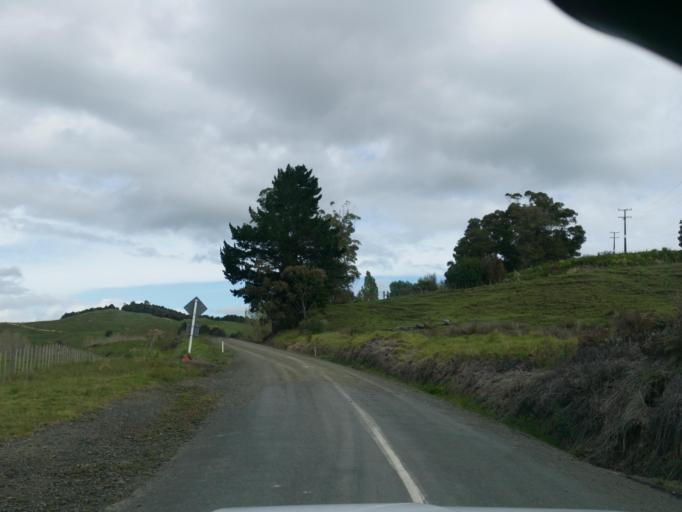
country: NZ
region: Northland
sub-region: Kaipara District
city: Dargaville
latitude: -35.9015
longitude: 173.9982
